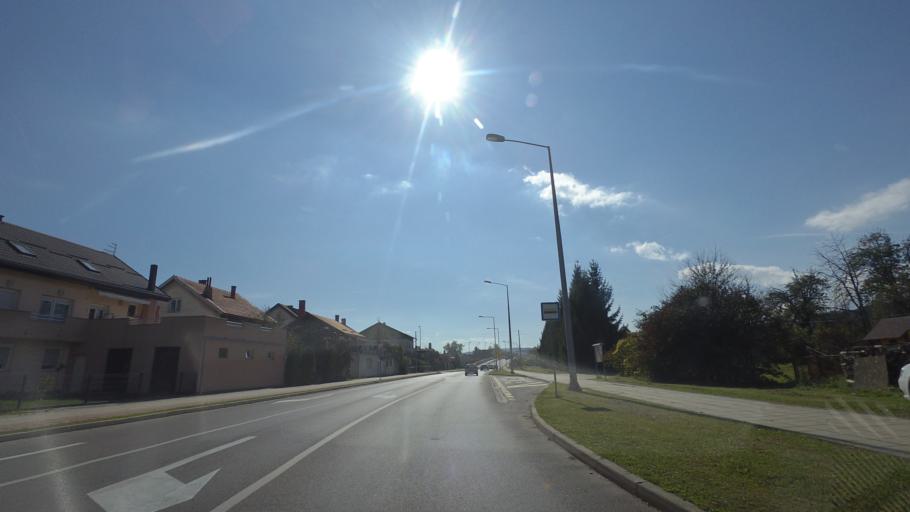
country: HR
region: Karlovacka
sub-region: Grad Karlovac
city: Karlovac
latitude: 45.4968
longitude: 15.5412
